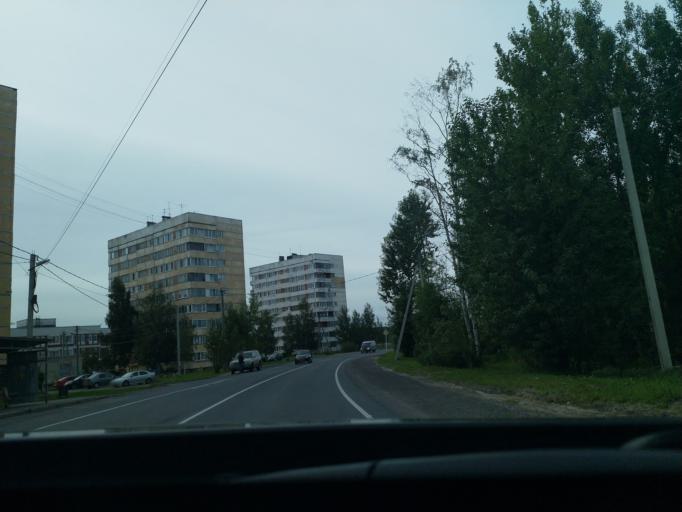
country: RU
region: Leningrad
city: Nikol'skoye
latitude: 59.7094
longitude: 30.7812
